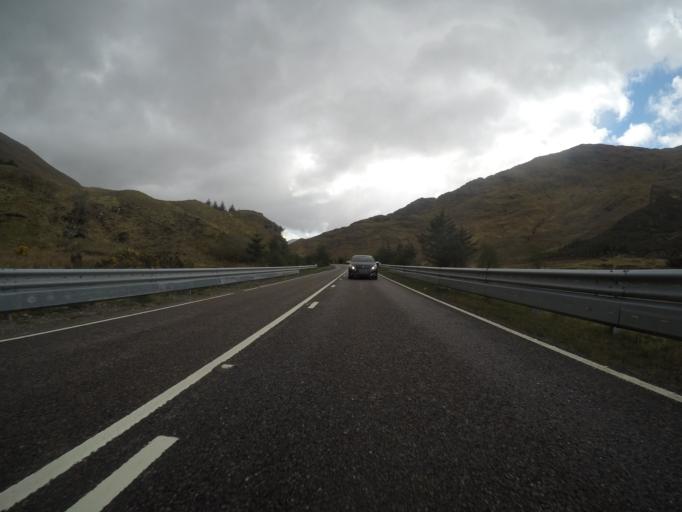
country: GB
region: Scotland
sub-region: Highland
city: Fort William
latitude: 57.1689
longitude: -5.2942
